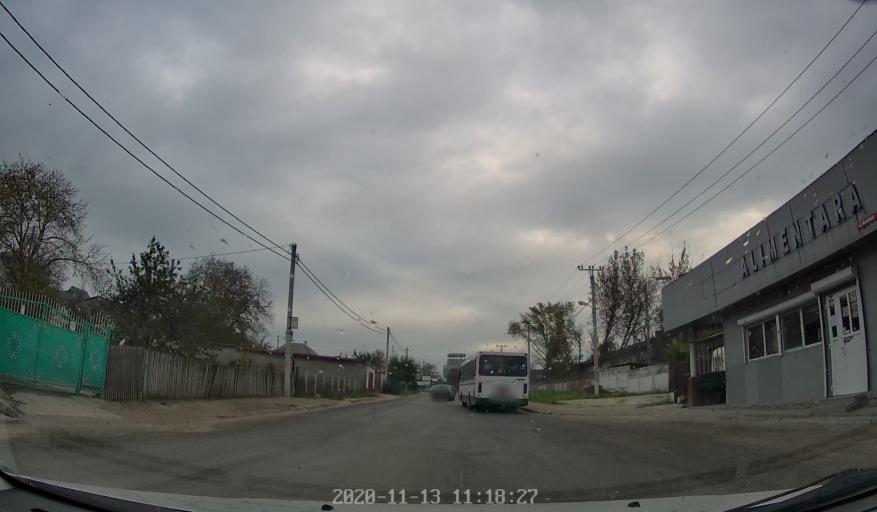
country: MD
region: Chisinau
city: Chisinau
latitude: 46.9908
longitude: 28.9127
